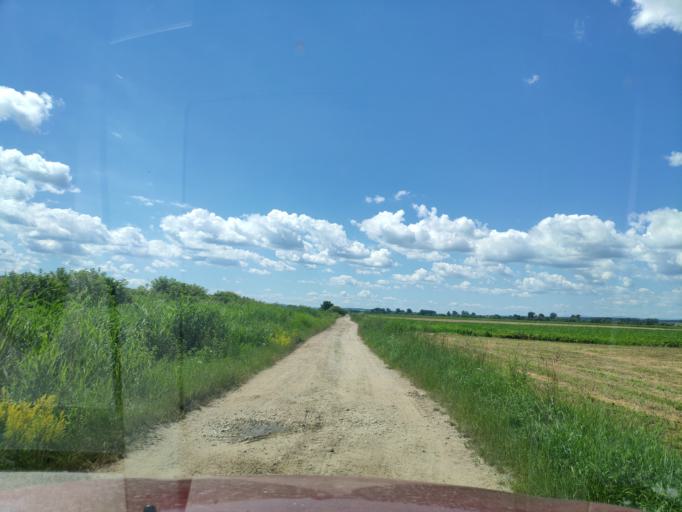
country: HU
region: Borsod-Abauj-Zemplen
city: Ozd
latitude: 48.2849
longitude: 20.2084
